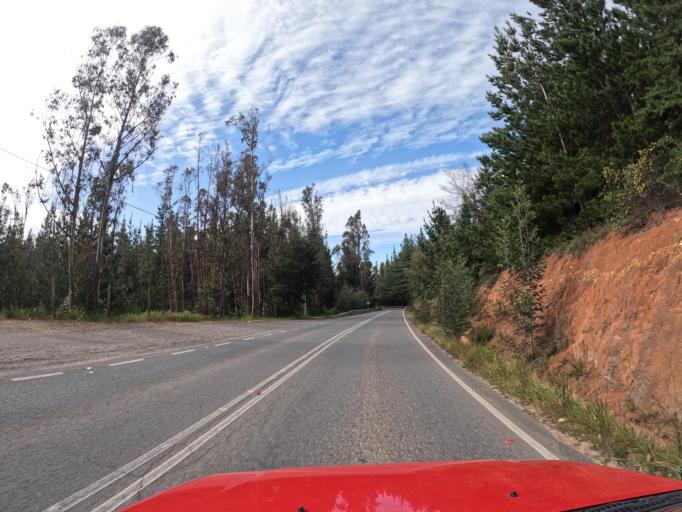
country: CL
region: O'Higgins
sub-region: Provincia de Colchagua
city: Santa Cruz
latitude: -34.3489
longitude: -71.8708
